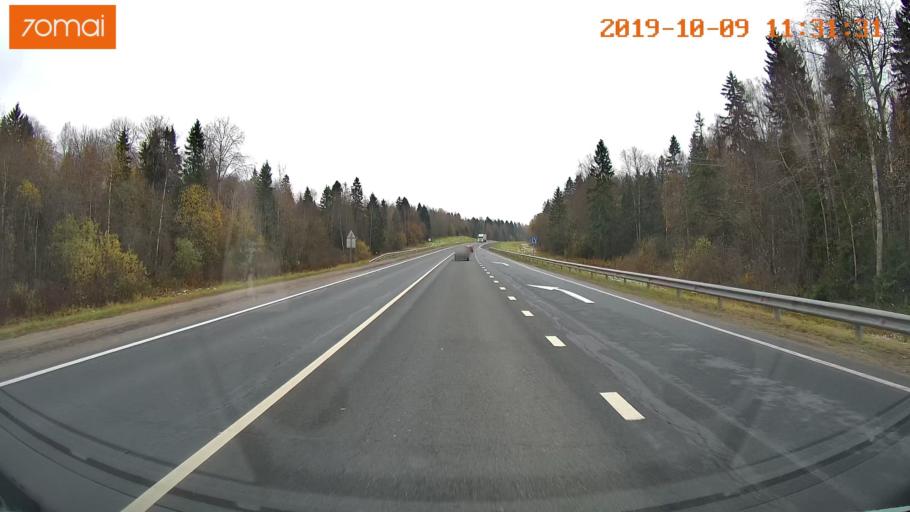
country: RU
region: Vologda
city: Gryazovets
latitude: 59.0447
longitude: 40.0978
